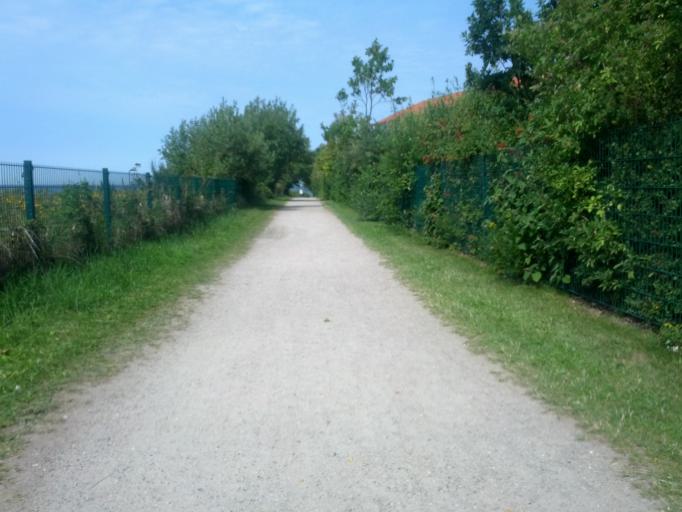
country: DE
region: Mecklenburg-Vorpommern
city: Bastorf
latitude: 54.1517
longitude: 11.7076
